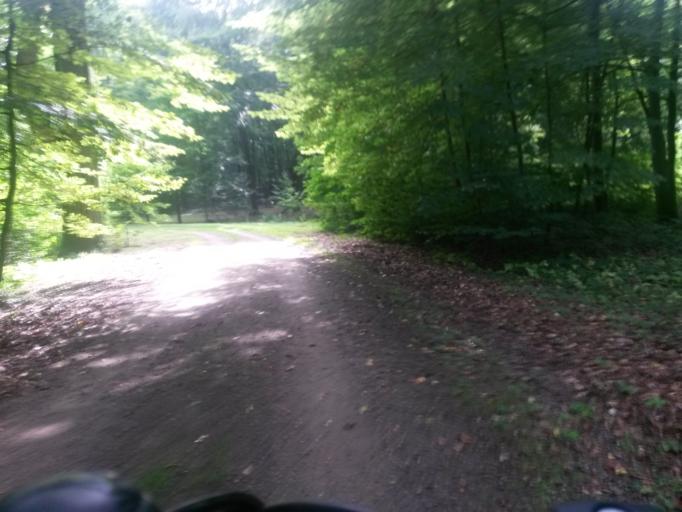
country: DE
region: Brandenburg
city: Angermunde
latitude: 53.0598
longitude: 13.9589
